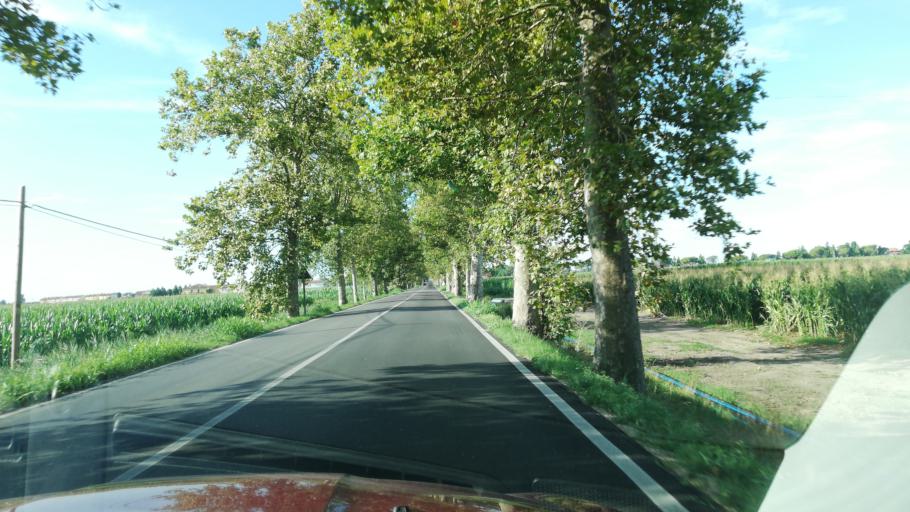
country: IT
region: Veneto
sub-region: Provincia di Venezia
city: La Salute di Livenza
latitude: 45.6661
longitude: 12.8038
